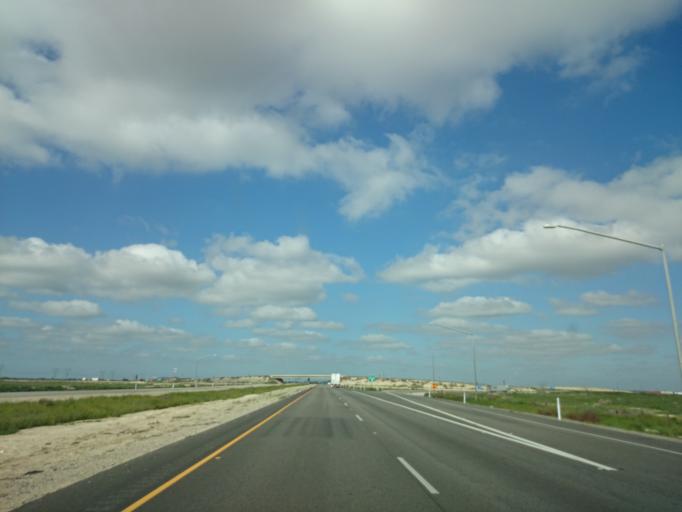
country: US
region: California
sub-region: Kern County
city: Rosedale
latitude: 35.2637
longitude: -119.2207
